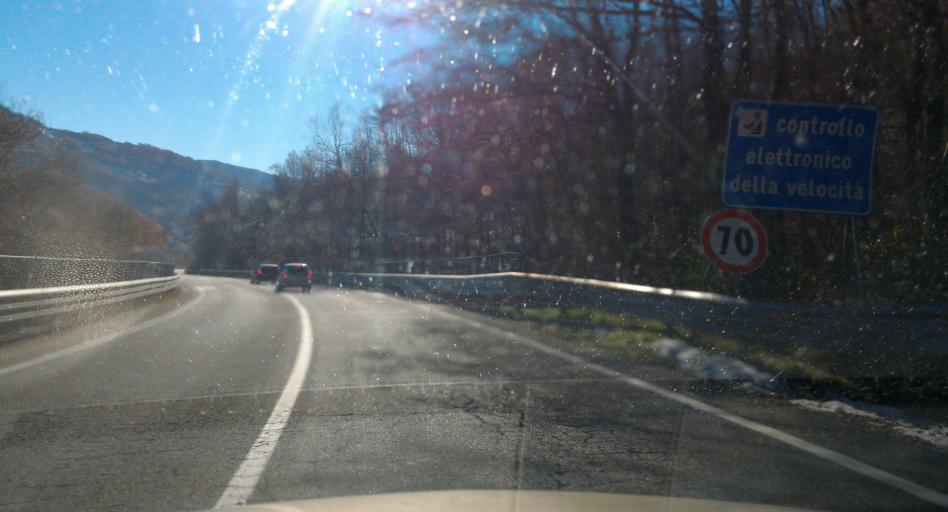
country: IT
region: Calabria
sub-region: Provincia di Cosenza
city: Spezzano della Sila
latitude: 39.3037
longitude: 16.3543
